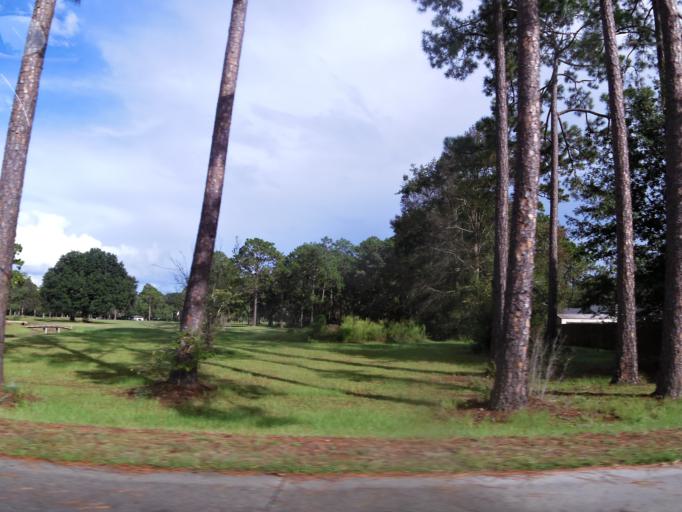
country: US
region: Georgia
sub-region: Liberty County
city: Walthourville
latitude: 31.7980
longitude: -81.6062
